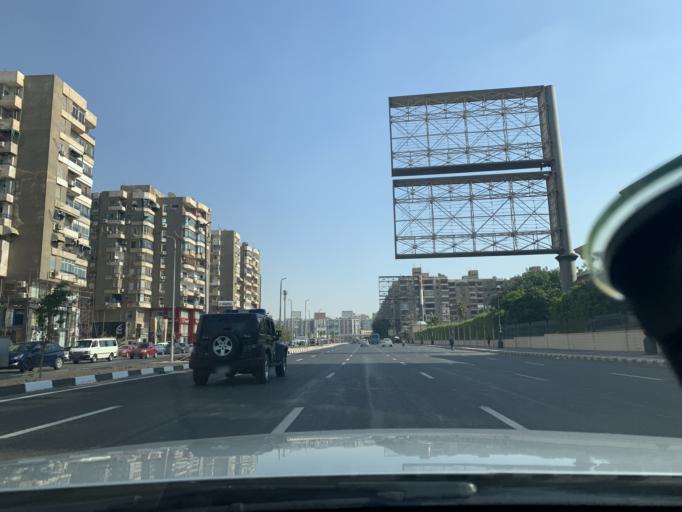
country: EG
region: Muhafazat al Qahirah
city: Cairo
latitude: 30.0768
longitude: 31.3394
